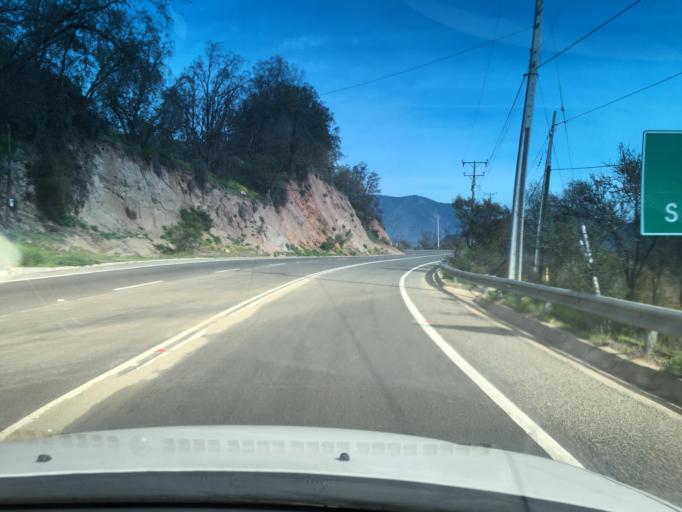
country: CL
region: Valparaiso
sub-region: Provincia de San Felipe
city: Llaillay
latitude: -33.0625
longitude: -71.0224
